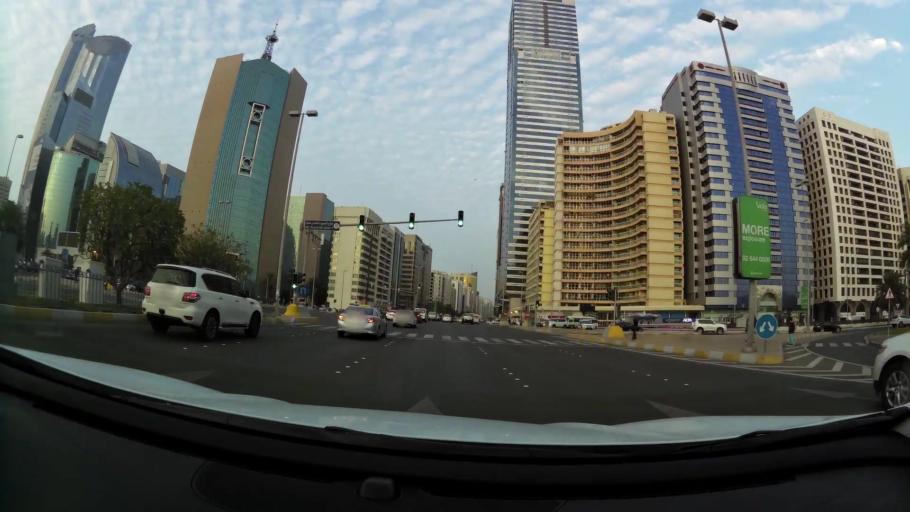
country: AE
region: Abu Dhabi
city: Abu Dhabi
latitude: 24.4823
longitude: 54.3587
